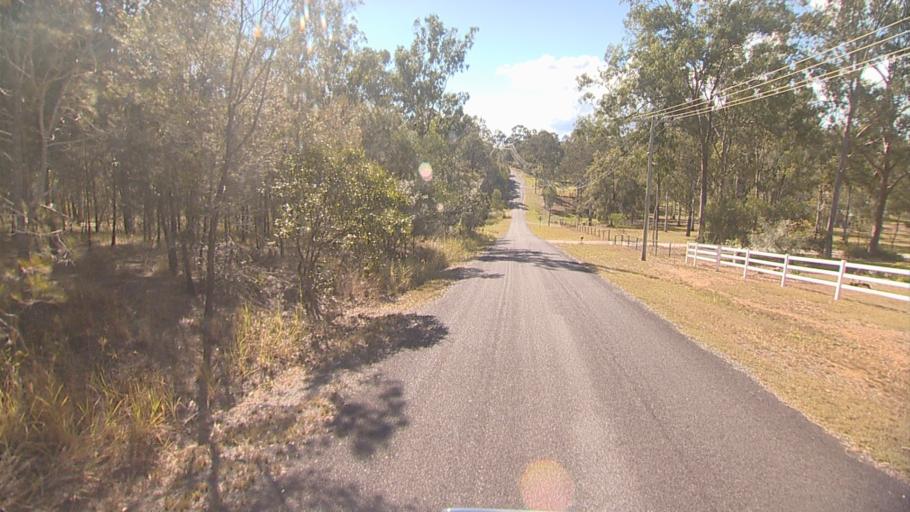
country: AU
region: Queensland
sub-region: Logan
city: Chambers Flat
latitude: -27.8135
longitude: 153.0890
